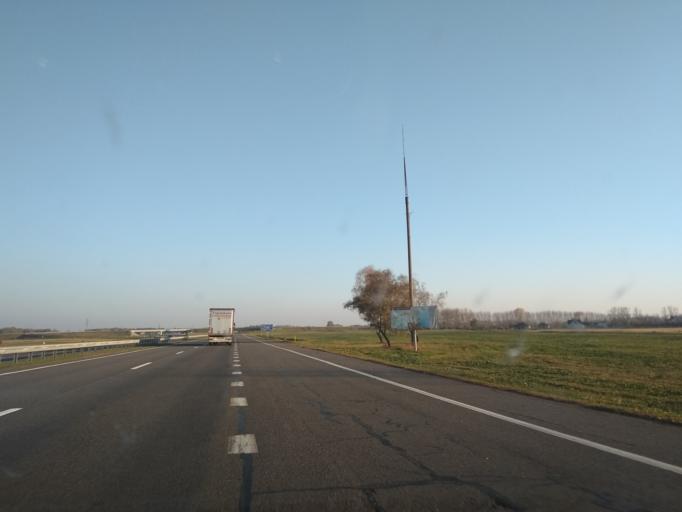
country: BY
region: Brest
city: Kobryn
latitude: 52.1854
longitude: 24.3201
